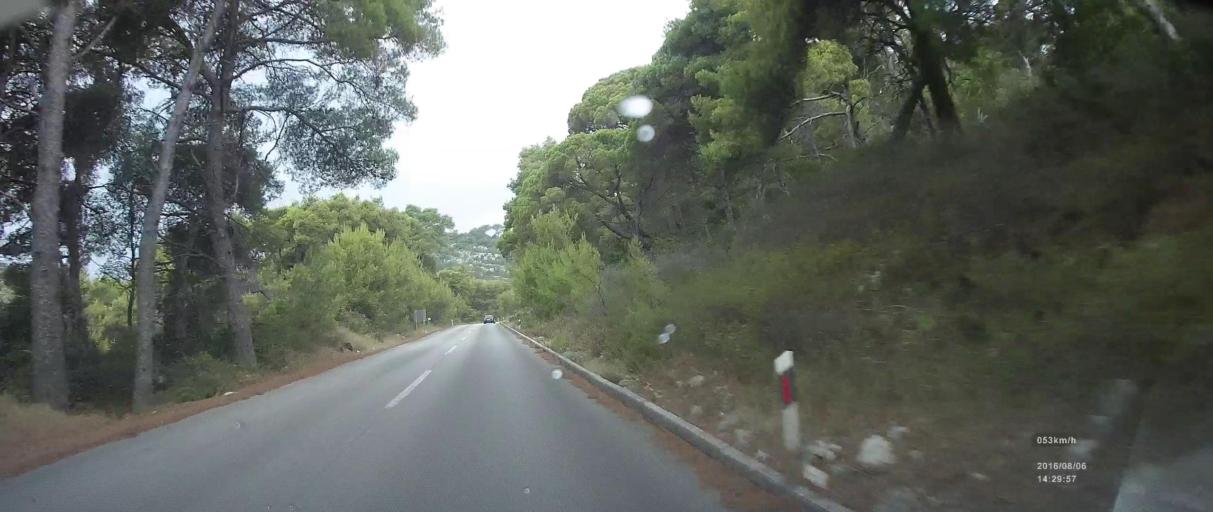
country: HR
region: Dubrovacko-Neretvanska
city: Ston
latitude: 42.7076
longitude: 17.7311
